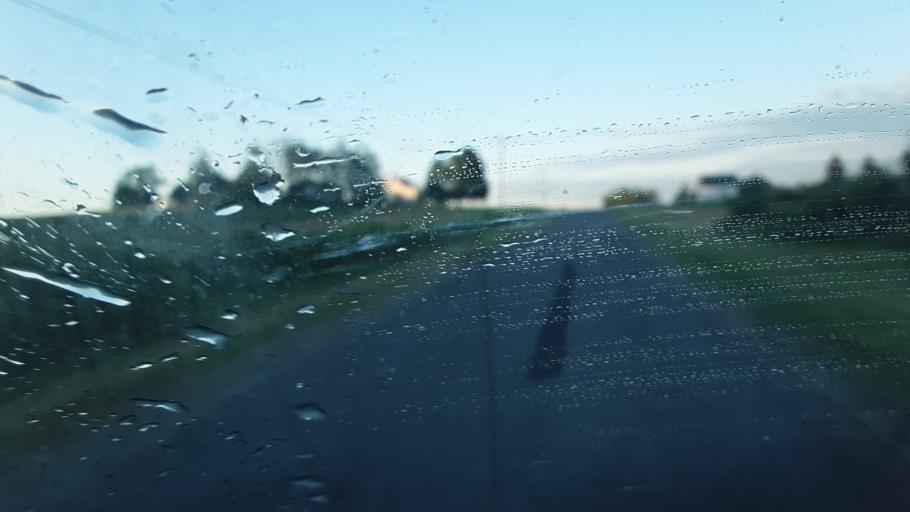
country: US
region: Maine
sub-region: Aroostook County
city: Caribou
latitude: 46.8225
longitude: -68.1355
